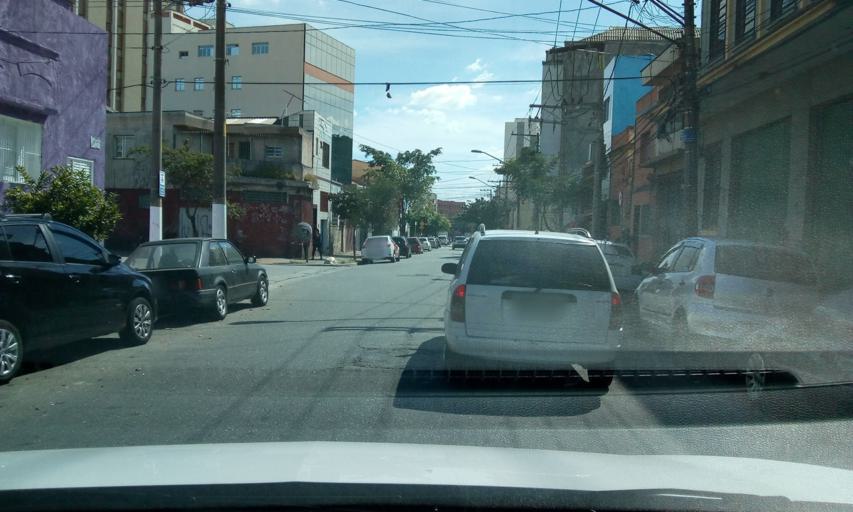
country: BR
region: Sao Paulo
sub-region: Sao Paulo
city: Sao Paulo
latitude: -23.5405
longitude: -46.6028
